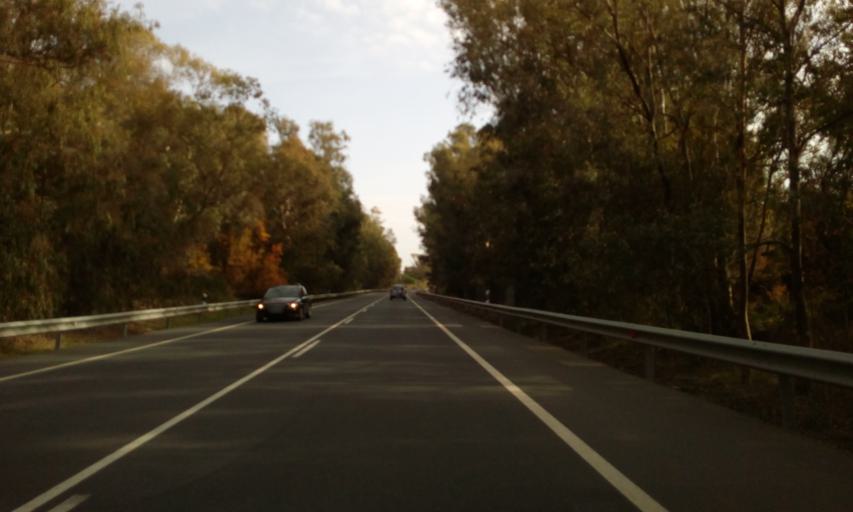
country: ES
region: Andalusia
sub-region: Provincia de Huelva
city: Palos de la Frontera
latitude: 37.1623
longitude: -6.8865
